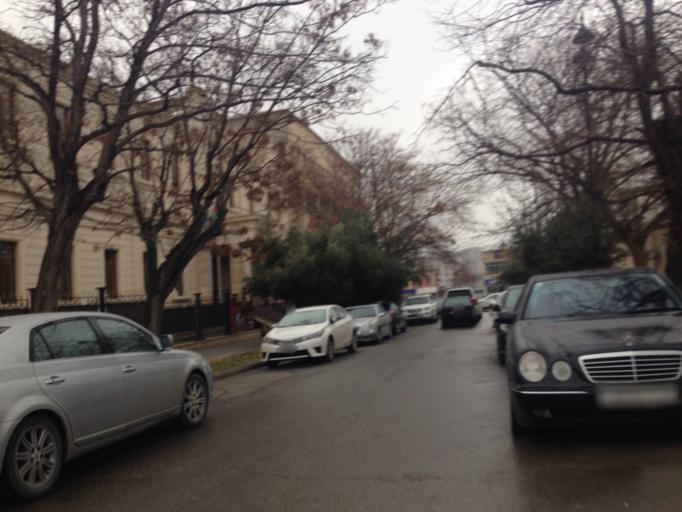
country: AZ
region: Baki
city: Baku
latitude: 40.3864
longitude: 49.8539
